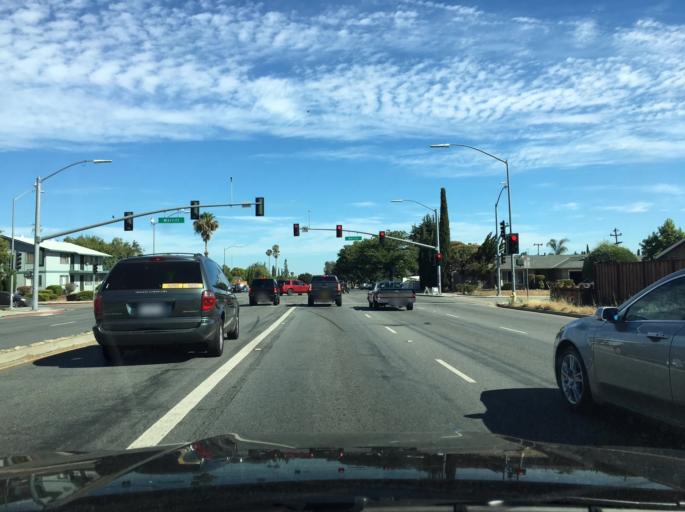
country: US
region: California
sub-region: Santa Clara County
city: Cambrian Park
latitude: 37.2425
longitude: -121.9054
